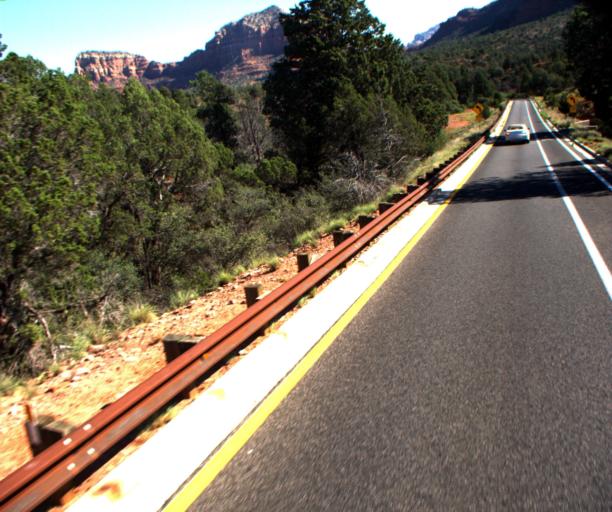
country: US
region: Arizona
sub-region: Yavapai County
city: Village of Oak Creek (Big Park)
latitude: 34.8090
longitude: -111.7664
